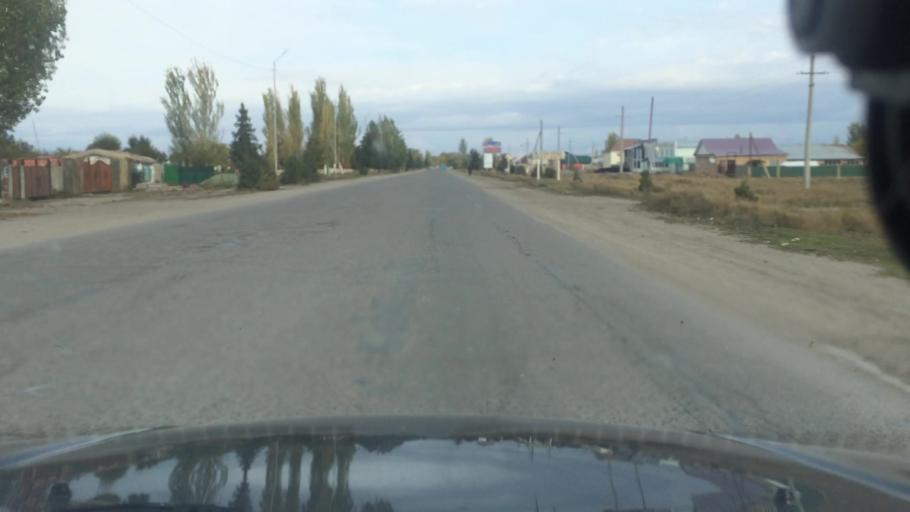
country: KG
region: Ysyk-Koel
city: Karakol
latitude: 42.5236
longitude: 78.3856
